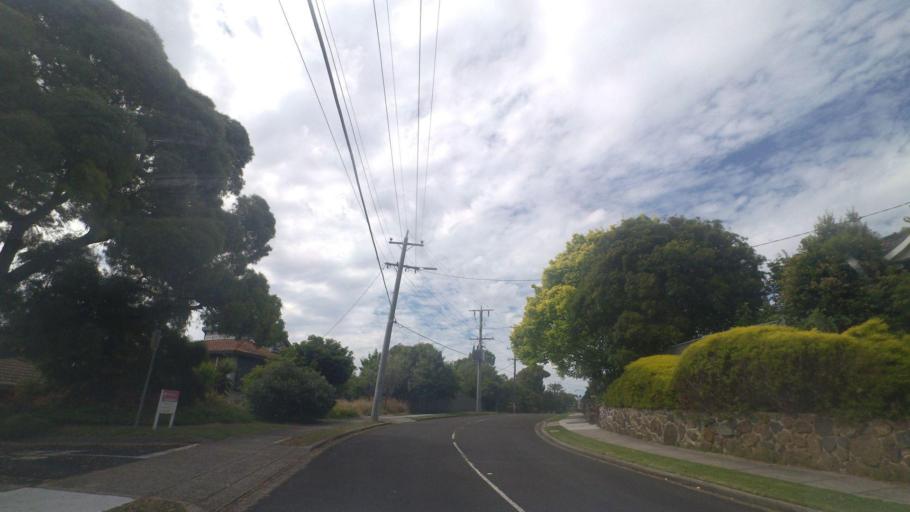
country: AU
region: Victoria
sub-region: Banyule
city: Viewbank
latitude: -37.7427
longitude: 145.0904
